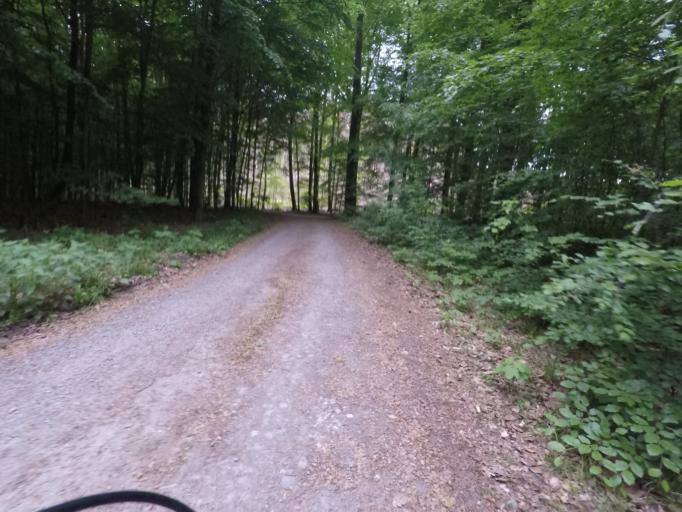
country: DE
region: North Rhine-Westphalia
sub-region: Regierungsbezirk Detmold
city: Bad Salzuflen
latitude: 52.1095
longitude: 8.7384
